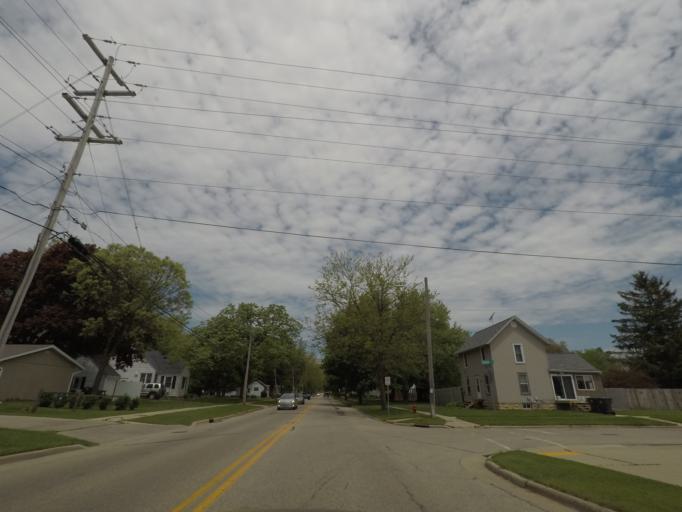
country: US
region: Wisconsin
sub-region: Rock County
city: Evansville
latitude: 42.7729
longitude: -89.2991
